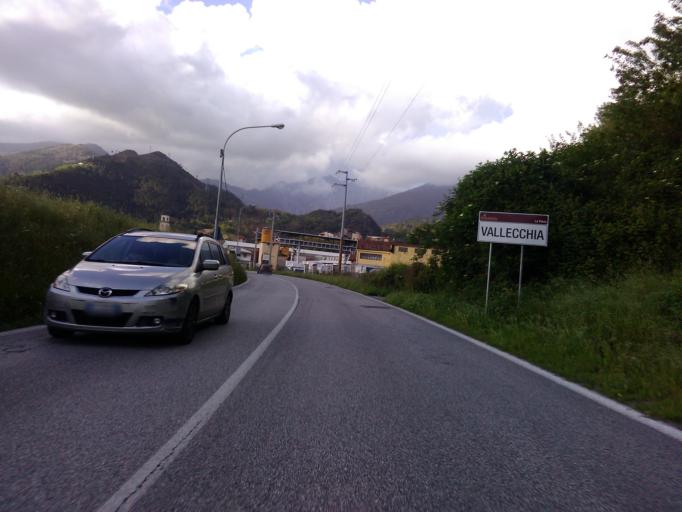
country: IT
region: Tuscany
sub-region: Provincia di Lucca
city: Ripa-Pozzi-Querceta-Ponterosso
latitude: 43.9775
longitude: 10.2211
